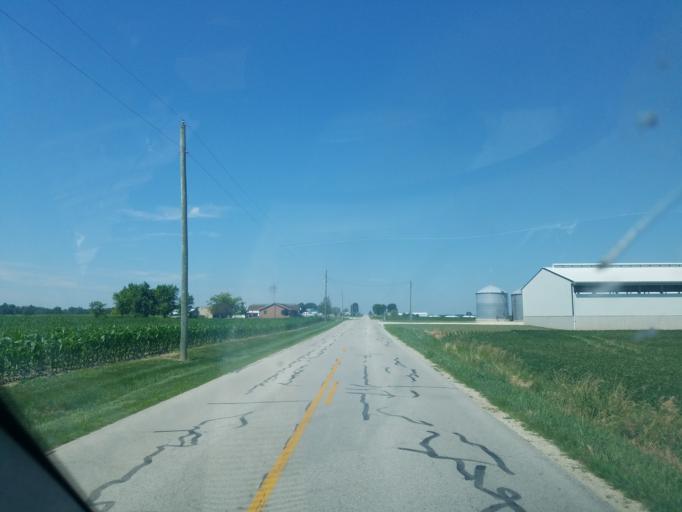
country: US
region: Ohio
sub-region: Mercer County
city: Saint Henry
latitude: 40.4506
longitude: -84.6920
